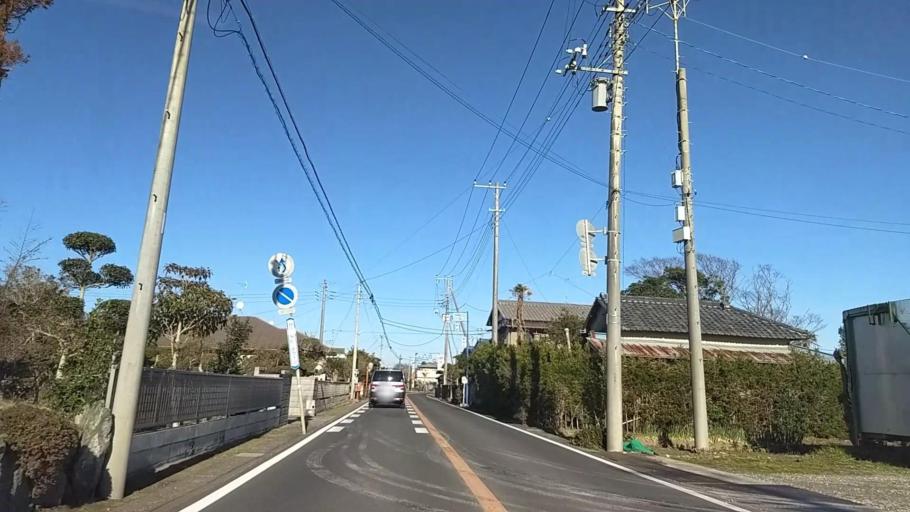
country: JP
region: Chiba
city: Naruto
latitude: 35.5502
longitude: 140.4623
